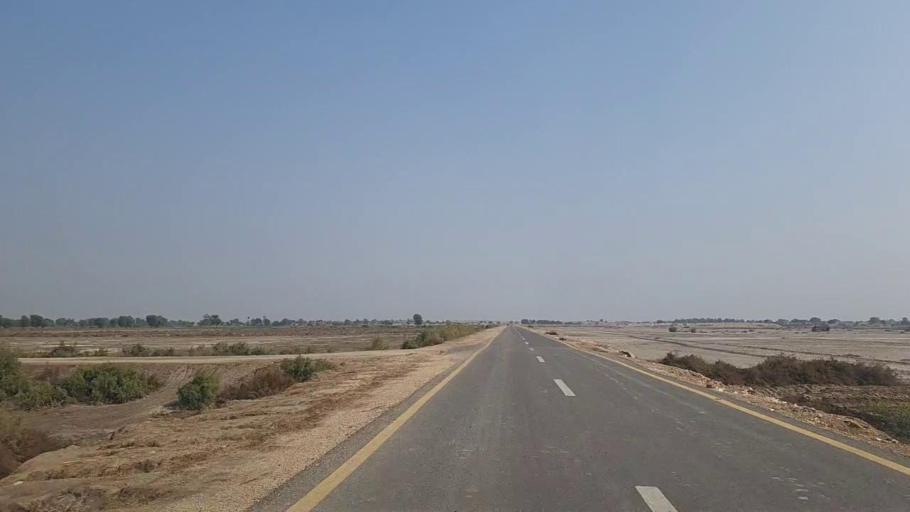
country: PK
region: Sindh
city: Jam Sahib
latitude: 26.3723
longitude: 68.5268
